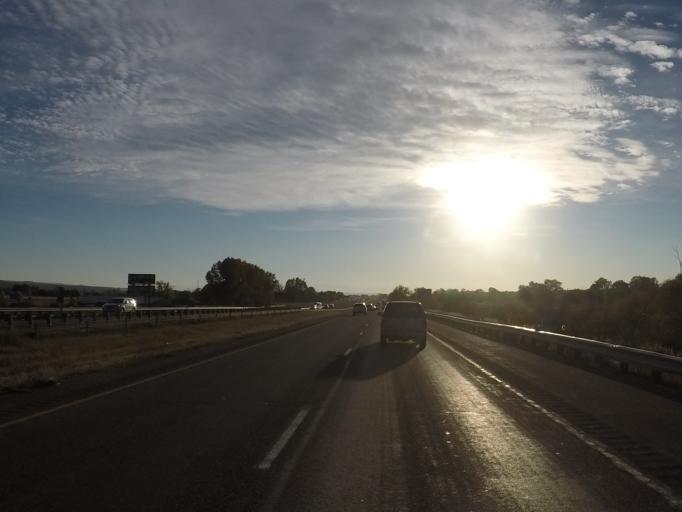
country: US
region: Montana
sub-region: Yellowstone County
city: Laurel
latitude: 45.7052
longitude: -108.6599
